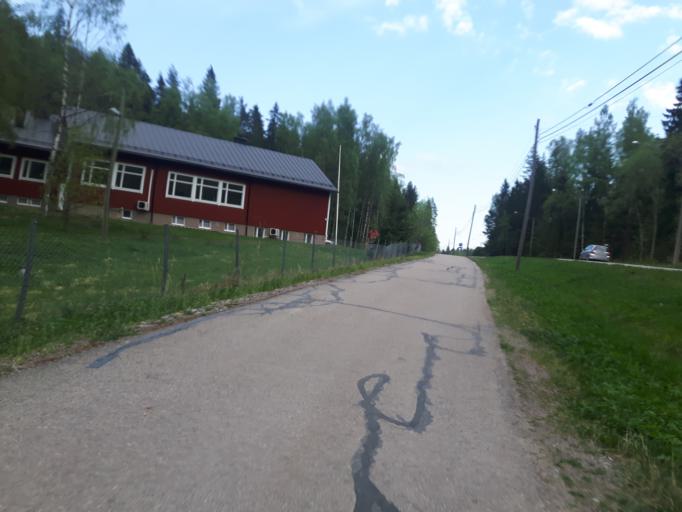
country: FI
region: Uusimaa
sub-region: Porvoo
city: Porvoo
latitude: 60.3977
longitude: 25.7313
